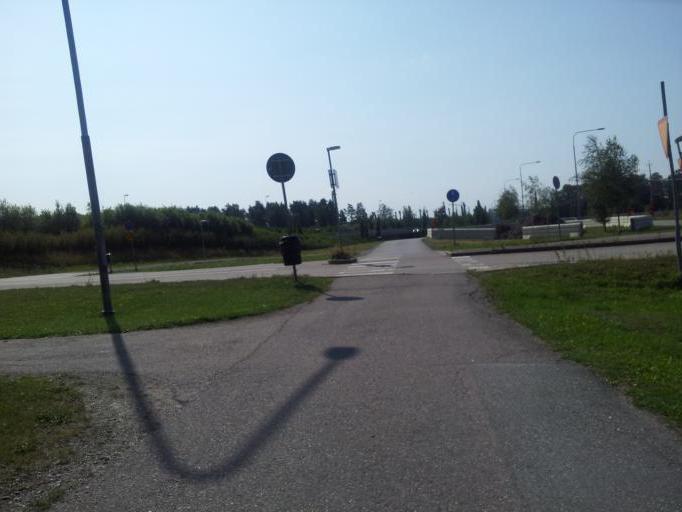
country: SE
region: Uppsala
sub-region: Uppsala Kommun
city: Gamla Uppsala
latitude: 59.8822
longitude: 17.6357
